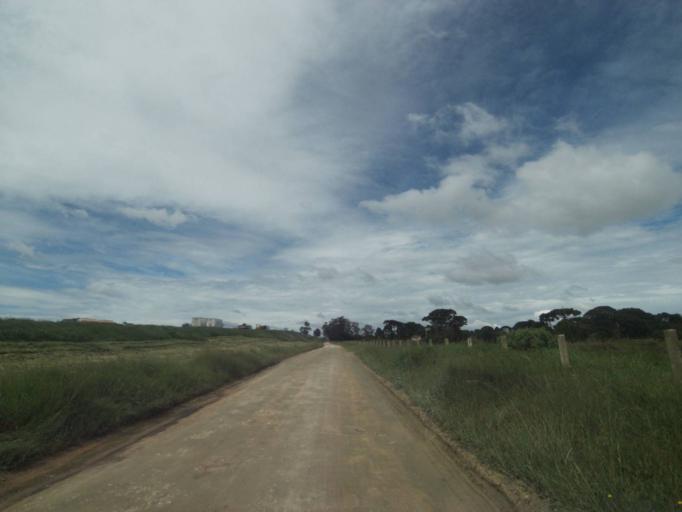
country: BR
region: Parana
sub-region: Sao Jose Dos Pinhais
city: Sao Jose dos Pinhais
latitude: -25.5303
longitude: -49.1439
